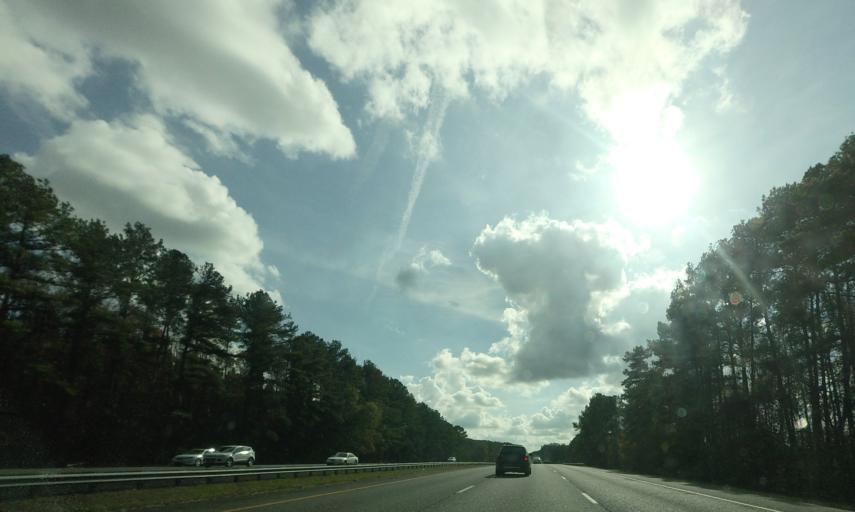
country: US
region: Georgia
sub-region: Houston County
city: Perry
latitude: 32.3978
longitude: -83.7658
